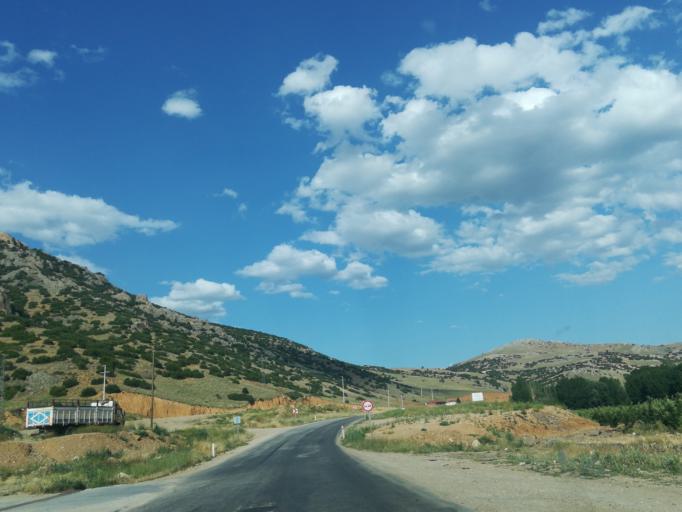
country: TR
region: Afyonkarahisar
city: Dinar
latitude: 38.0994
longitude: 30.1505
